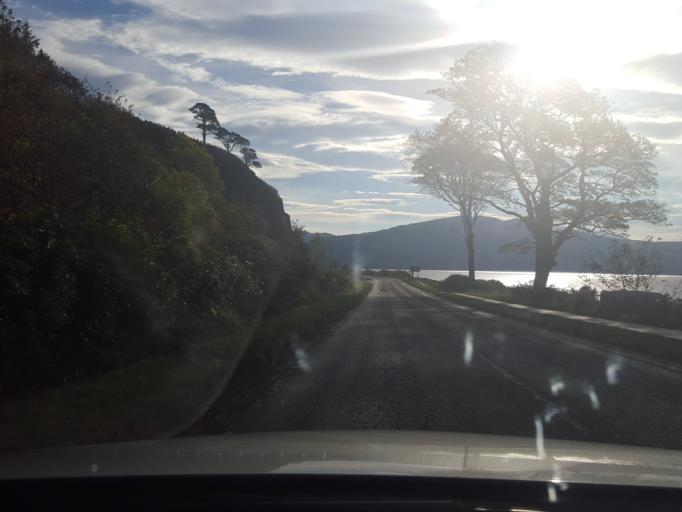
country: GB
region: Scotland
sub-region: Highland
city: Portree
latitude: 57.2854
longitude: -5.6407
